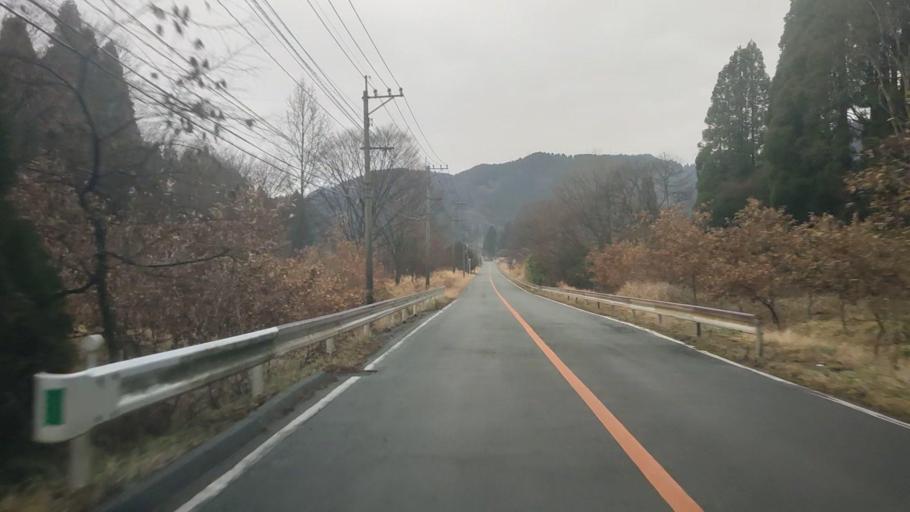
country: JP
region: Kumamoto
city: Aso
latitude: 32.8597
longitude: 131.1624
